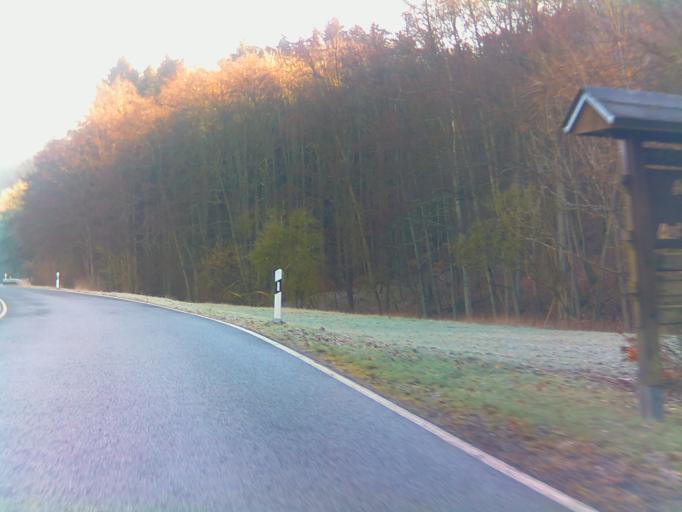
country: DE
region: Rheinland-Pfalz
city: Auen
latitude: 49.8310
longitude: 7.6018
